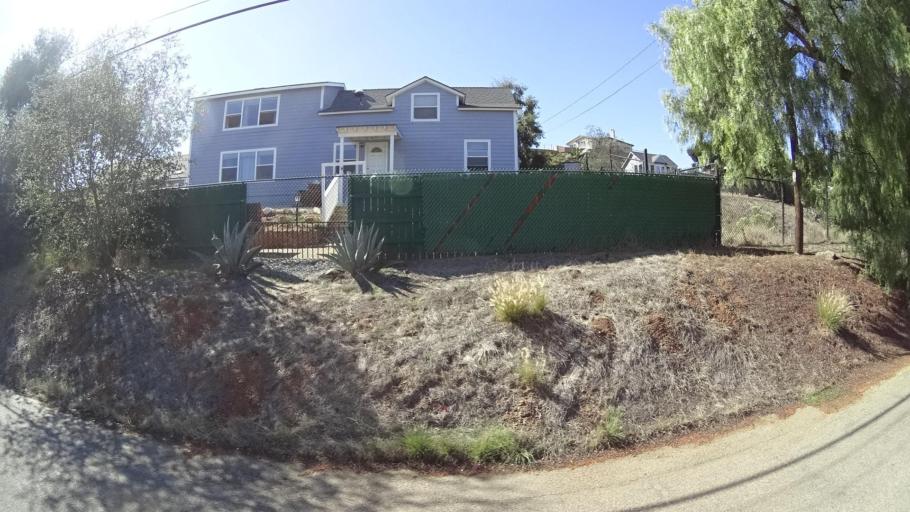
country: US
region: California
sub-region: San Diego County
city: La Presa
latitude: 32.6872
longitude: -117.0154
